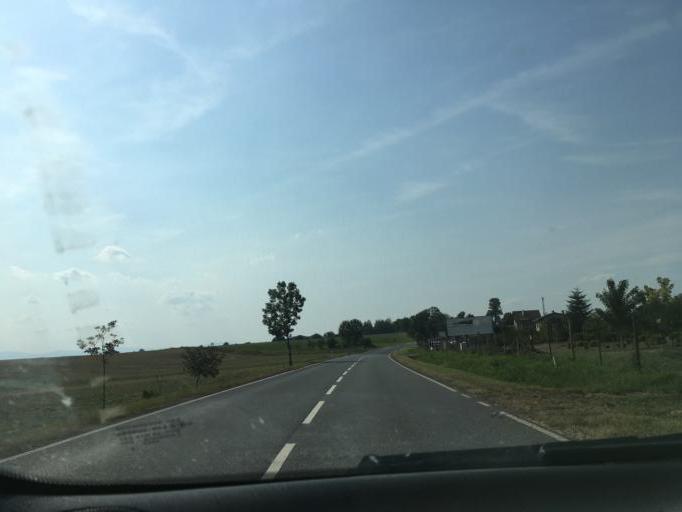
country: PL
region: Opole Voivodeship
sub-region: Powiat nyski
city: Nysa
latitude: 50.4230
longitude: 17.4429
